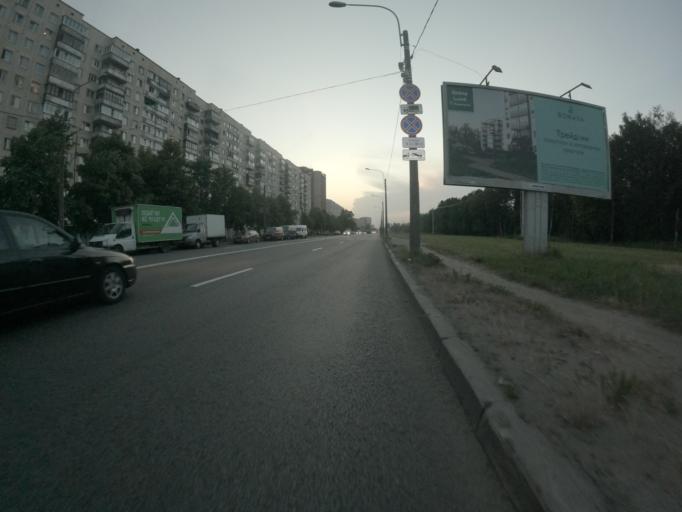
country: RU
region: St.-Petersburg
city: Krasnogvargeisky
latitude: 59.9471
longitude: 30.5044
